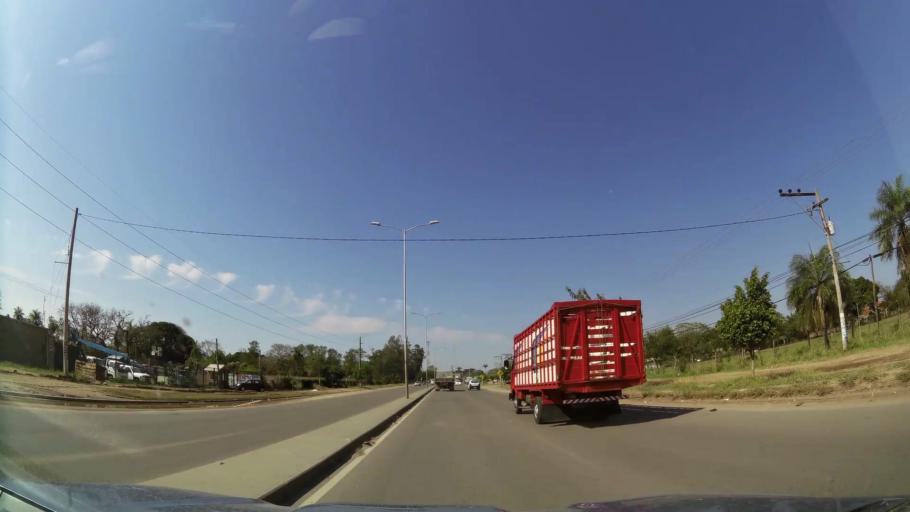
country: BO
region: Santa Cruz
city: Cotoca
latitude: -17.7650
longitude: -63.1030
